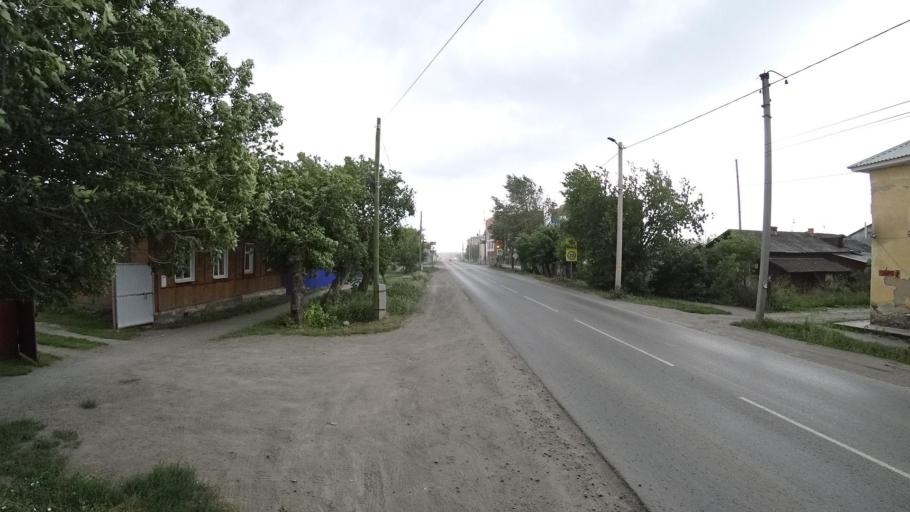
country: RU
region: Sverdlovsk
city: Kamyshlov
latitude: 56.8500
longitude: 62.7004
